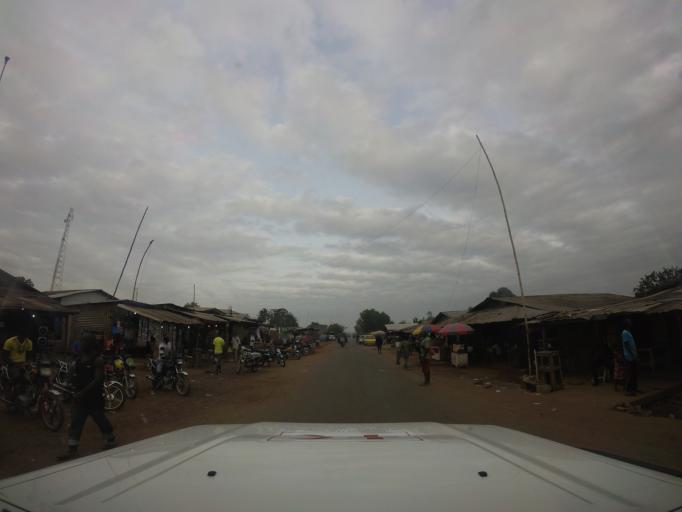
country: LR
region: Bomi
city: Tubmanburg
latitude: 6.7150
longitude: -10.9722
